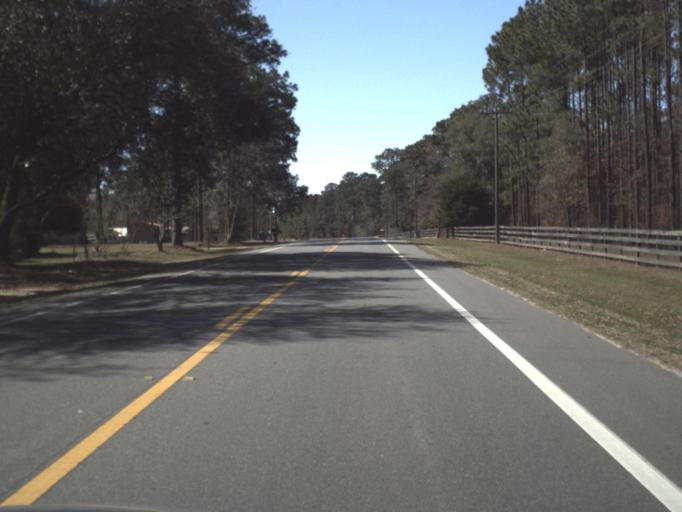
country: US
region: Florida
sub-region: Gadsden County
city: Chattahoochee
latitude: 30.6994
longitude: -84.7715
